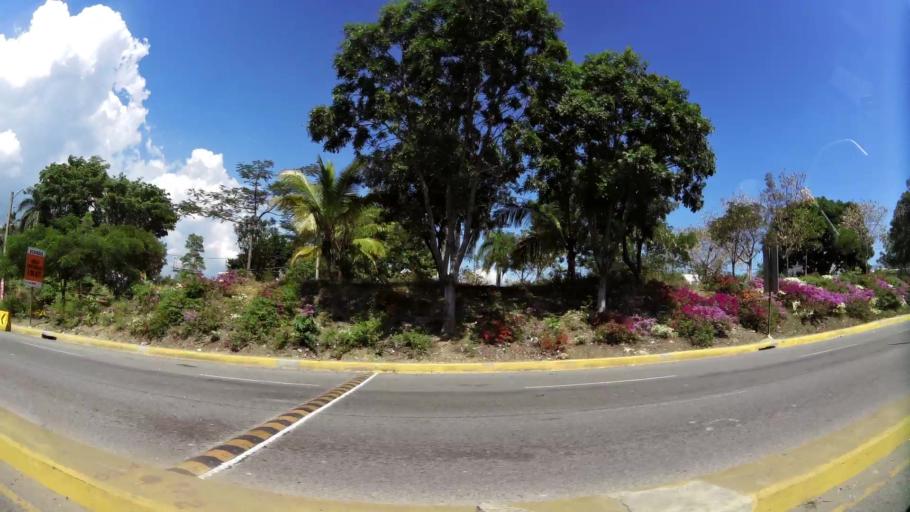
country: DO
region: Nacional
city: Bella Vista
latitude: 18.4540
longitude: -69.9806
